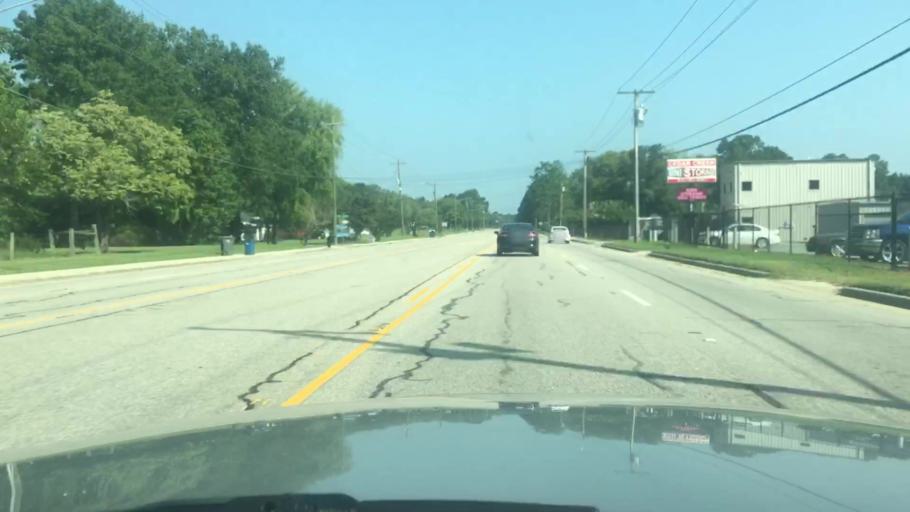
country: US
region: North Carolina
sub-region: Cumberland County
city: Vander
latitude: 35.0150
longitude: -78.8373
